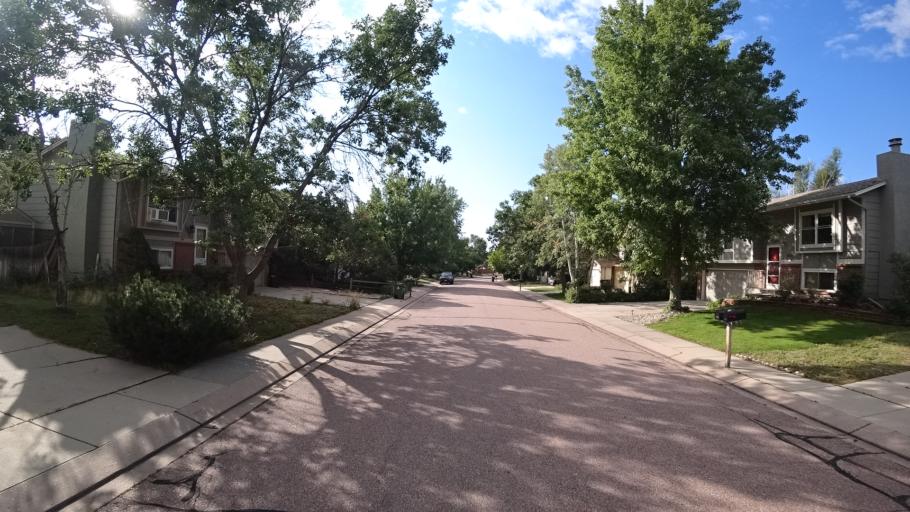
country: US
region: Colorado
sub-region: El Paso County
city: Air Force Academy
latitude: 38.9148
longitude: -104.8596
